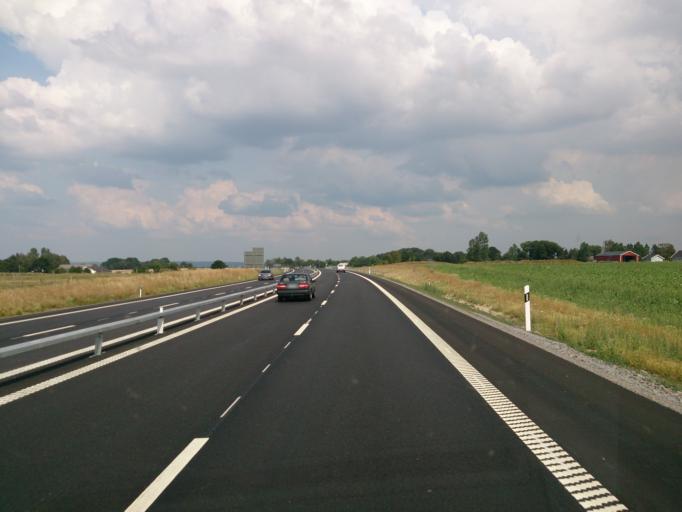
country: SE
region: Skane
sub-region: Hoors Kommun
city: Loberod
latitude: 55.8257
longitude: 13.5358
